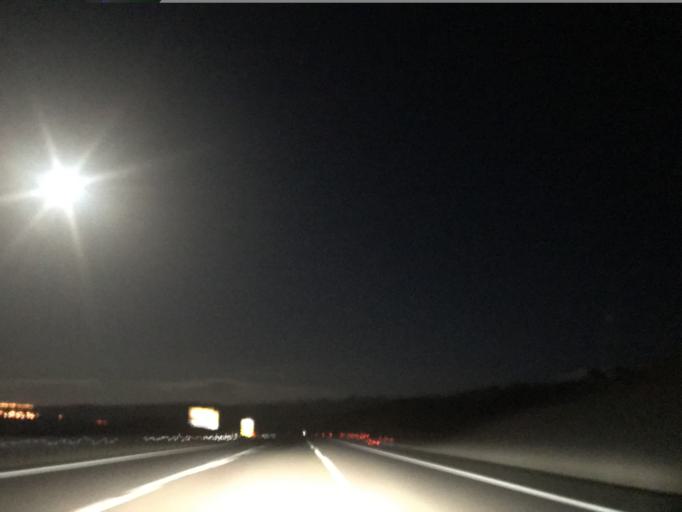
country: TR
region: Nigde
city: Ulukisla
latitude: 37.6329
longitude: 34.4514
